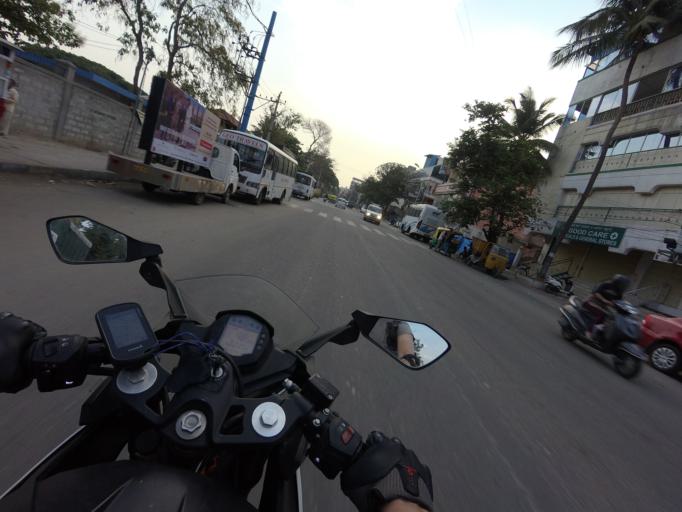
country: IN
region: Karnataka
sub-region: Bangalore Urban
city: Bangalore
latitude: 13.0182
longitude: 77.6366
